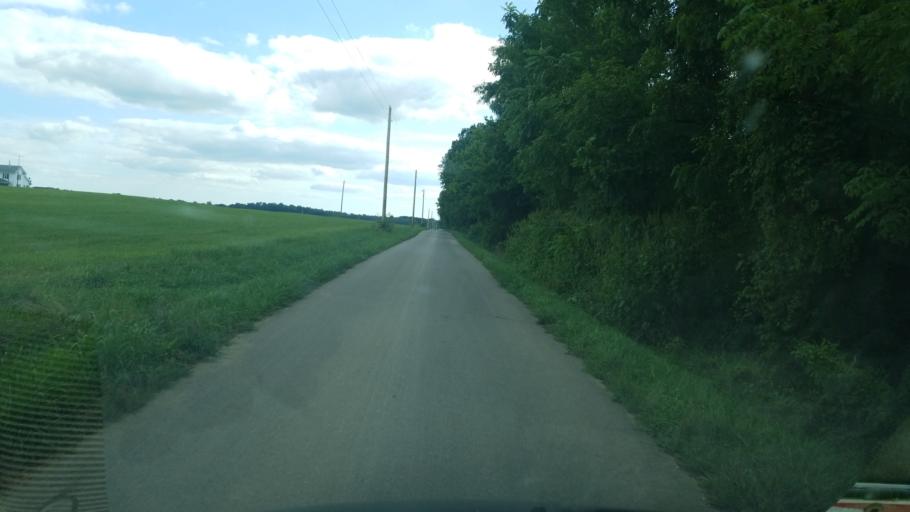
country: US
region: Ohio
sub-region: Logan County
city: De Graff
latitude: 40.3722
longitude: -83.8880
